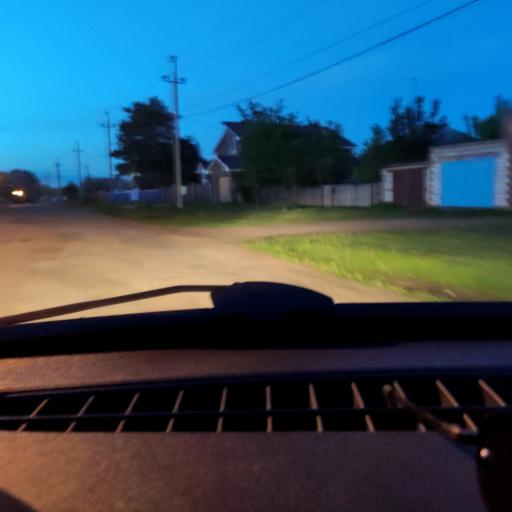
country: RU
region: Bashkortostan
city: Karmaskaly
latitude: 54.3686
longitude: 56.1626
